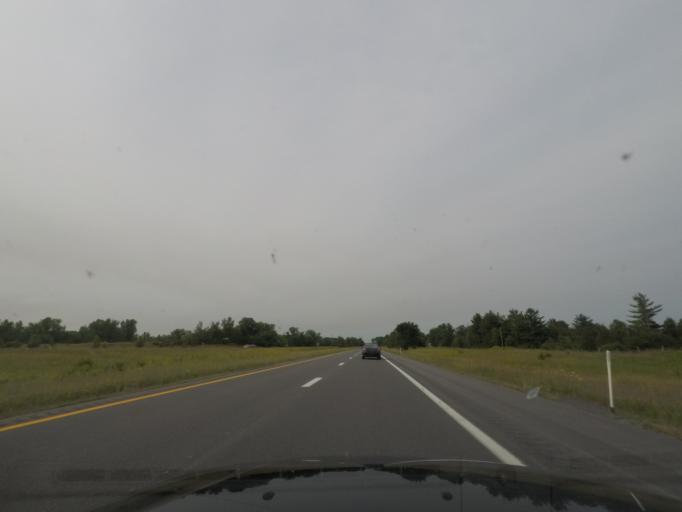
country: US
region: New York
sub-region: Clinton County
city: Cumberland Head
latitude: 44.8203
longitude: -73.4466
